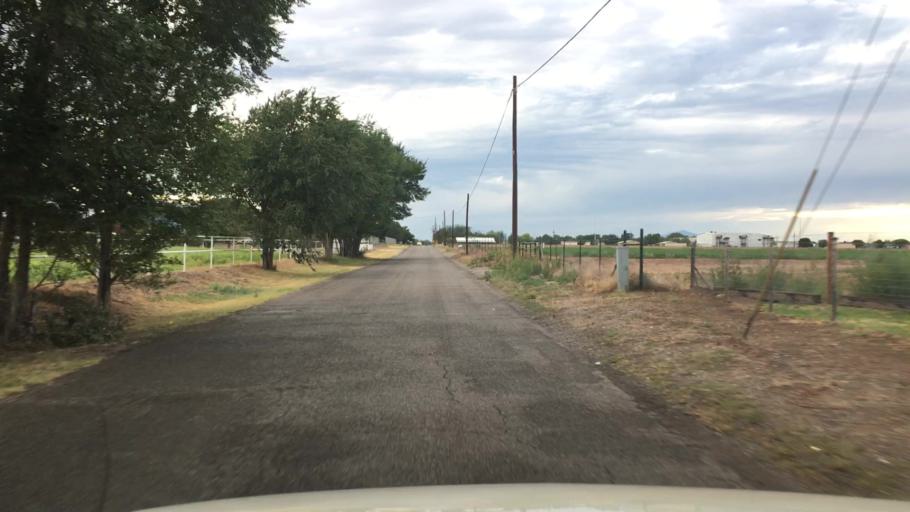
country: US
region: New Mexico
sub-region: Chaves County
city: Roswell
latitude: 33.4160
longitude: -104.4994
